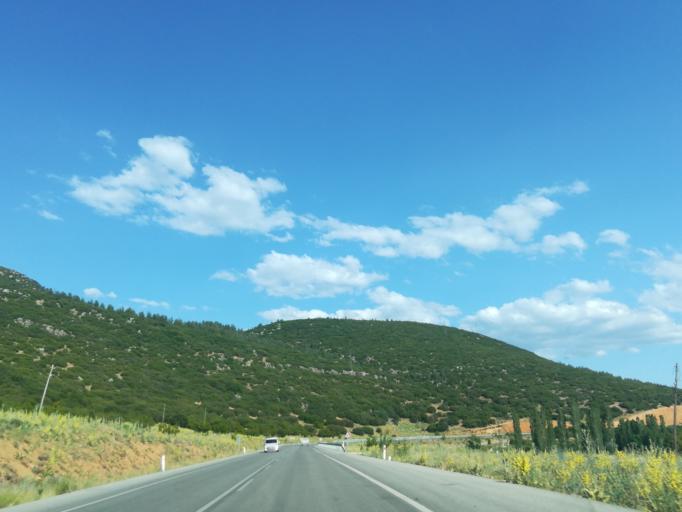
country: TR
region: Denizli
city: Ishakli
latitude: 38.1613
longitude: 30.0806
